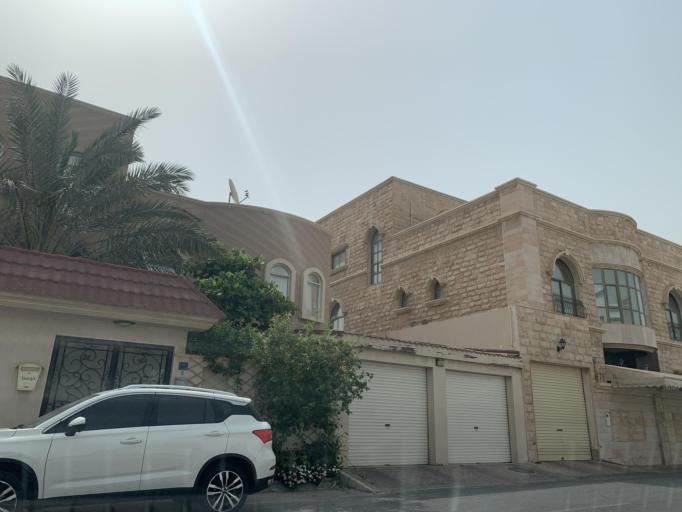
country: BH
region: Northern
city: Madinat `Isa
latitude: 26.1693
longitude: 50.5505
